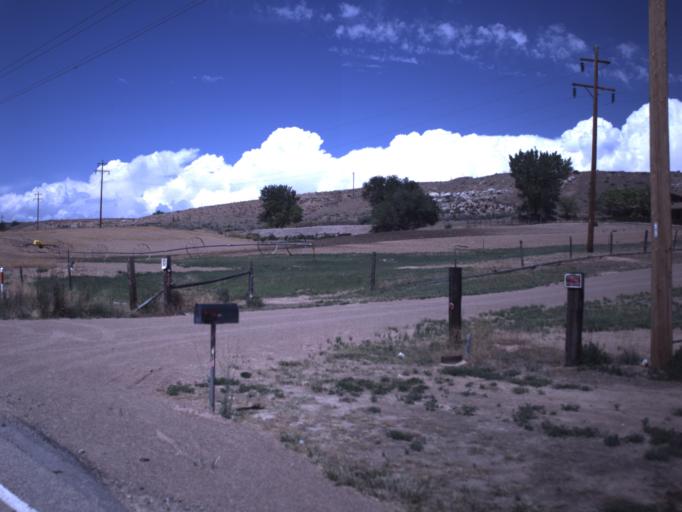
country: US
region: Utah
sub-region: Uintah County
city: Naples
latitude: 40.2153
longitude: -109.6757
